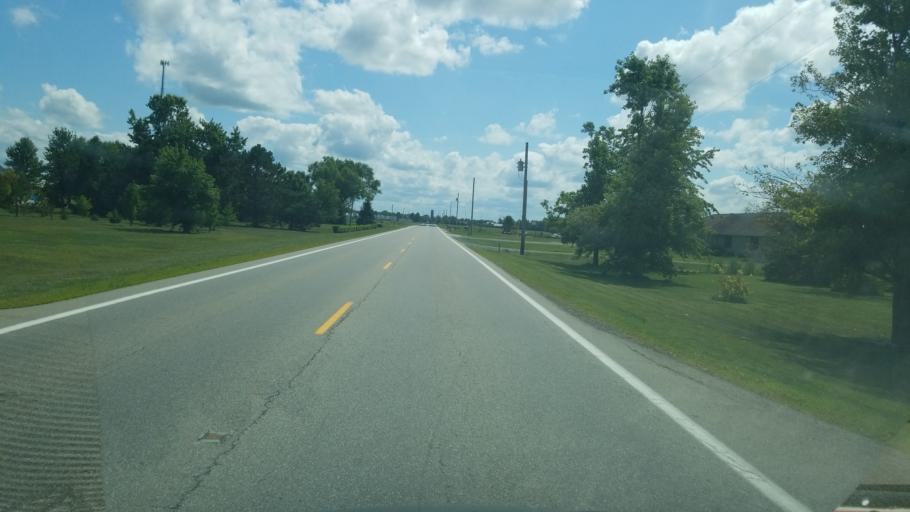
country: US
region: Ohio
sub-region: Putnam County
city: Kalida
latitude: 41.0043
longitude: -84.1980
